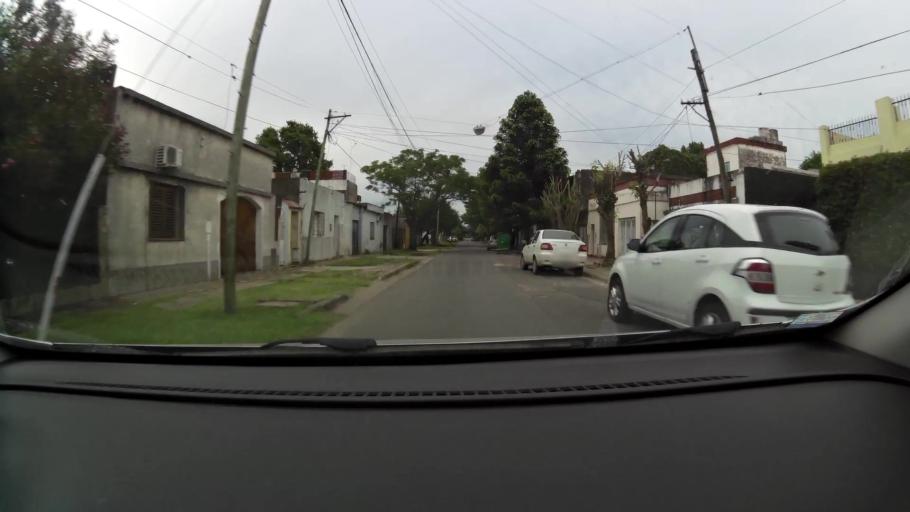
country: AR
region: Santa Fe
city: Granadero Baigorria
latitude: -32.8955
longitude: -60.6993
